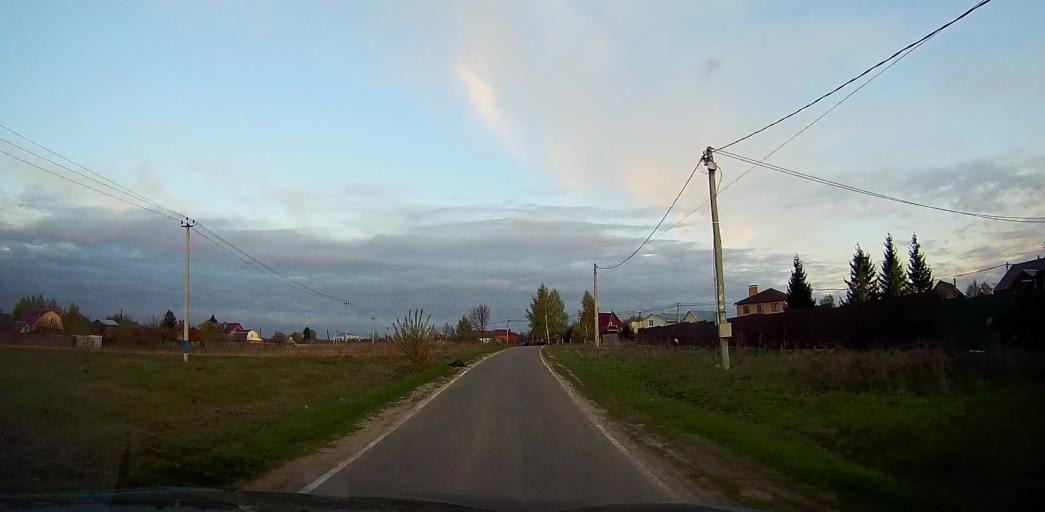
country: RU
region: Moskovskaya
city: Peski
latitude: 55.2130
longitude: 38.7395
